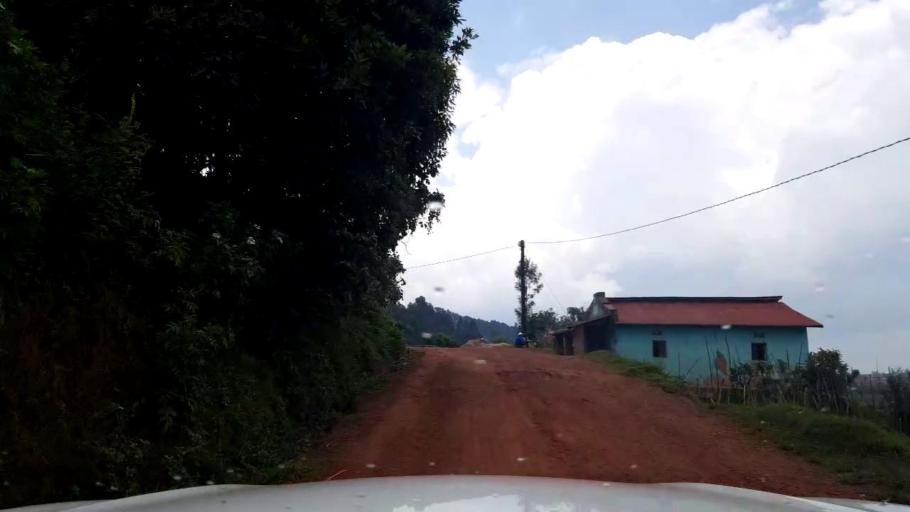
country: RW
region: Northern Province
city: Byumba
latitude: -1.5279
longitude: 29.9594
